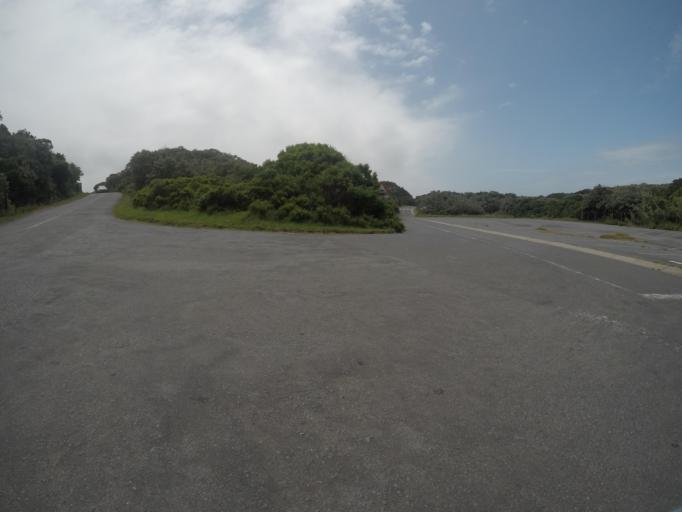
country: ZA
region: Eastern Cape
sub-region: Buffalo City Metropolitan Municipality
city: East London
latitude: -32.9954
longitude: 27.9471
